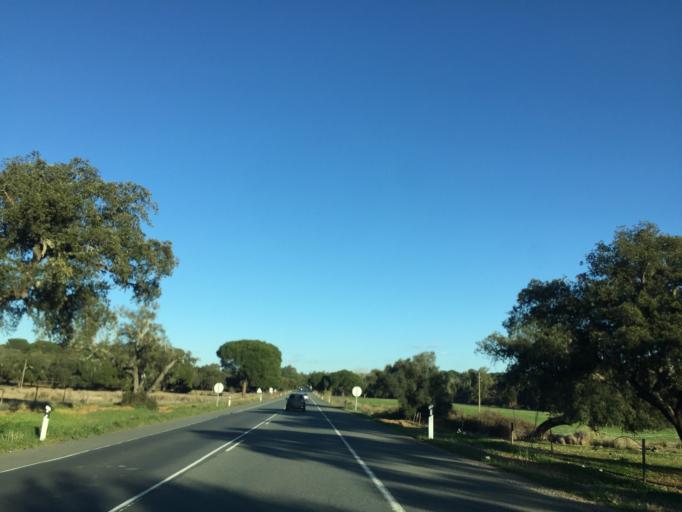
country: PT
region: Setubal
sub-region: Grandola
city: Grandola
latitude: 38.1213
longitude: -8.4411
